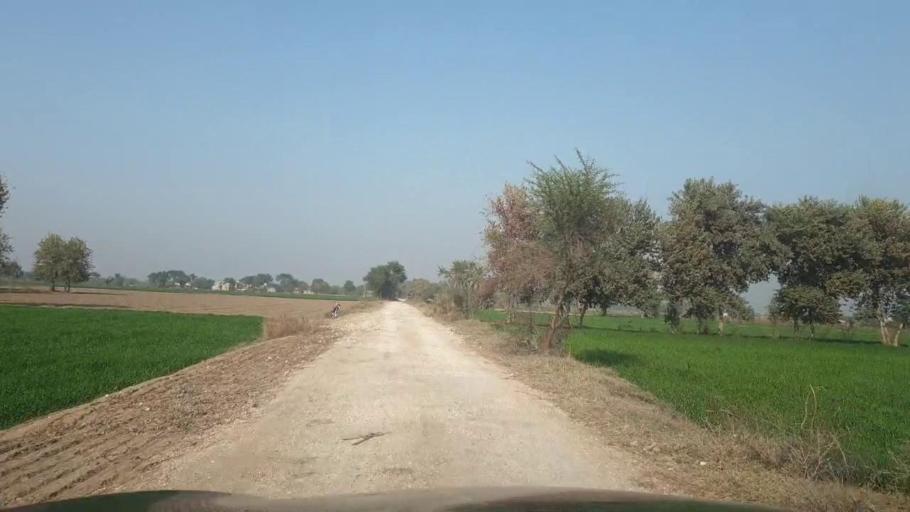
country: PK
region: Sindh
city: Ubauro
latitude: 28.0907
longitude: 69.8412
